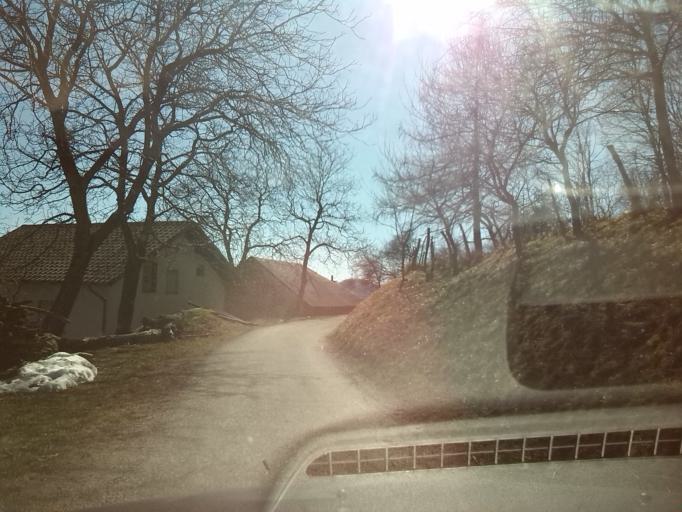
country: IT
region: Friuli Venezia Giulia
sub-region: Provincia di Udine
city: Cras
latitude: 46.2003
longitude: 13.5887
